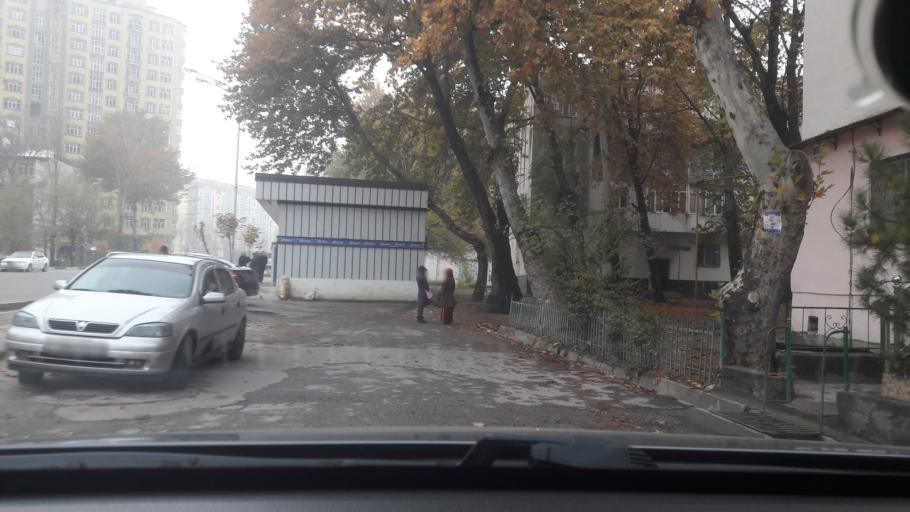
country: TJ
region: Dushanbe
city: Dushanbe
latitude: 38.5885
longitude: 68.7438
